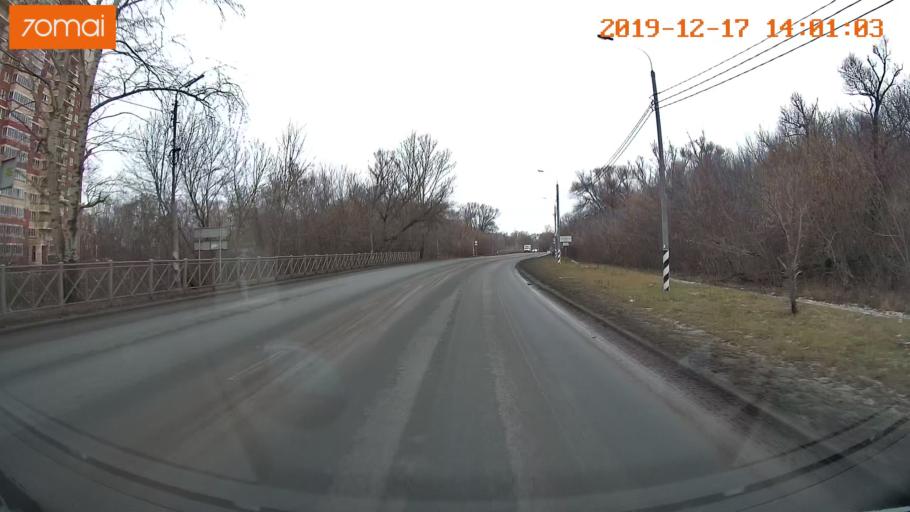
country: RU
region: Rjazan
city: Ryazan'
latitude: 54.6182
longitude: 39.6637
